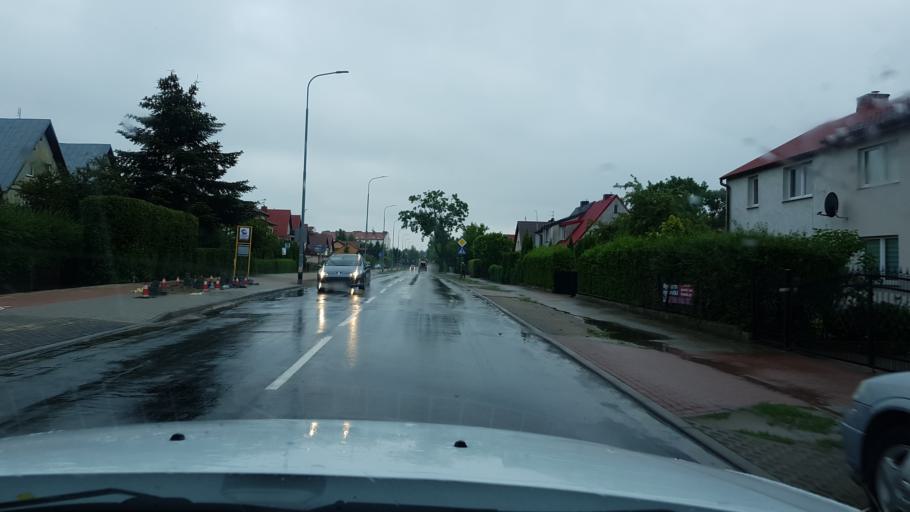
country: PL
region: West Pomeranian Voivodeship
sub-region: Powiat kolobrzeski
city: Kolobrzeg
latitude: 54.1575
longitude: 15.5455
